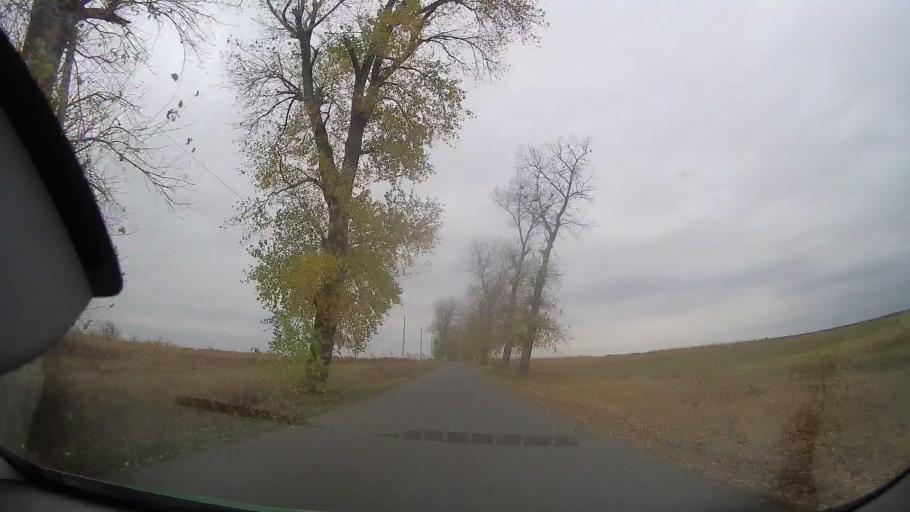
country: RO
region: Braila
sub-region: Comuna Ciocile
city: Ciocile
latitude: 44.8091
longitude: 27.2808
